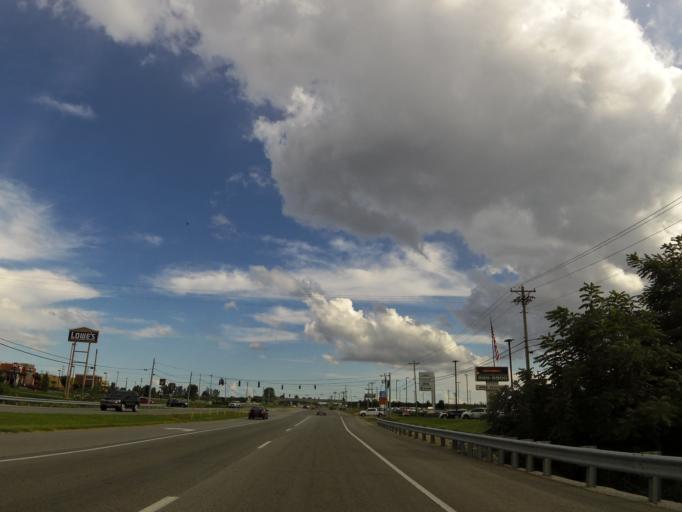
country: US
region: Kentucky
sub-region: Christian County
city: Hopkinsville
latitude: 36.8211
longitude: -87.4729
